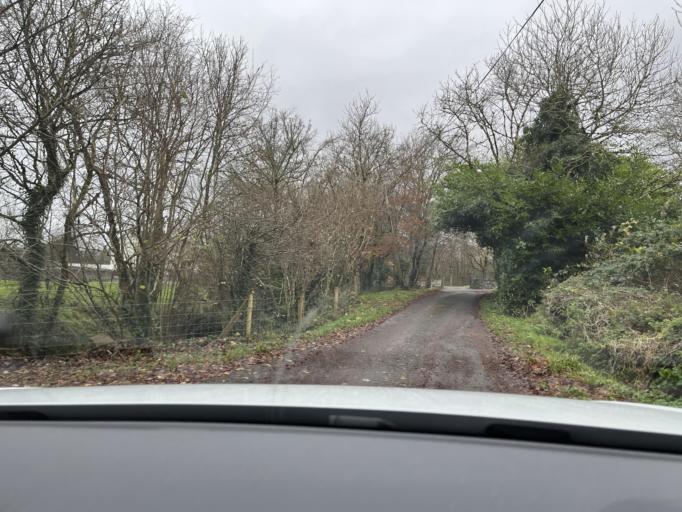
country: IE
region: Connaught
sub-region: County Leitrim
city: Manorhamilton
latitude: 54.2883
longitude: -8.1219
